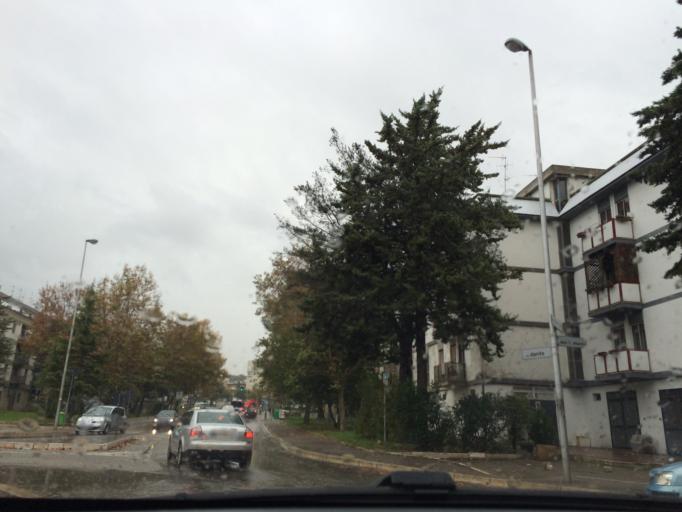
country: IT
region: Basilicate
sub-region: Provincia di Matera
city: Matera
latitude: 40.6764
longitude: 16.5884
